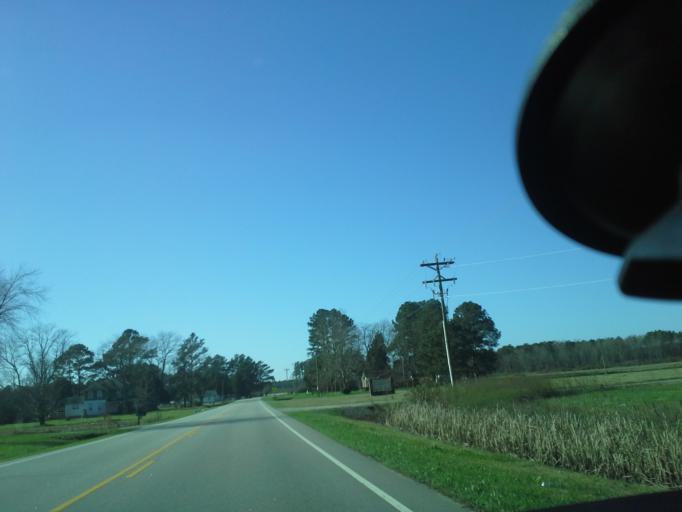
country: US
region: North Carolina
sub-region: Beaufort County
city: Belhaven
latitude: 35.5789
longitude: -76.6756
